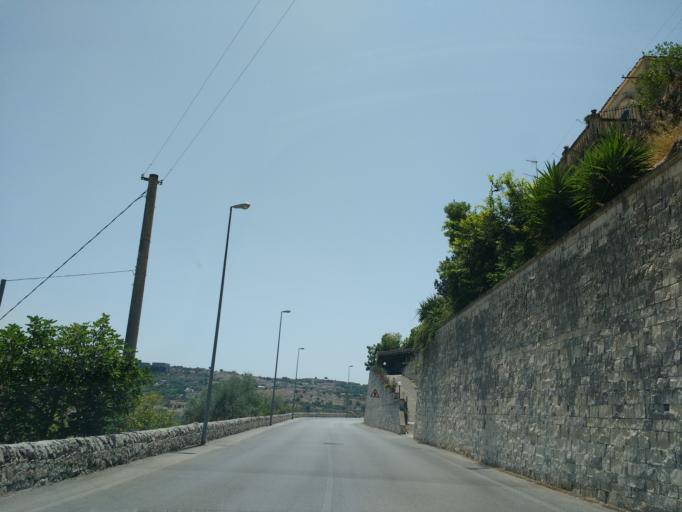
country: IT
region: Sicily
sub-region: Ragusa
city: Modica
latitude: 36.8652
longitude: 14.7559
